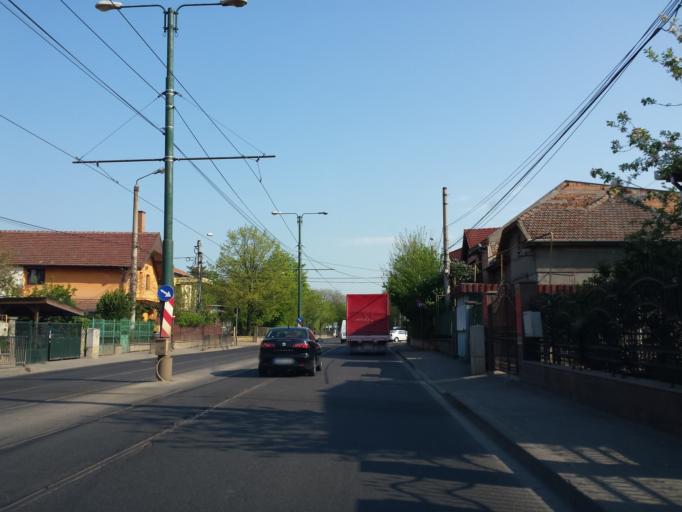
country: RO
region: Timis
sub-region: Comuna Dumbravita
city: Dumbravita
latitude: 45.7669
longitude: 21.2606
